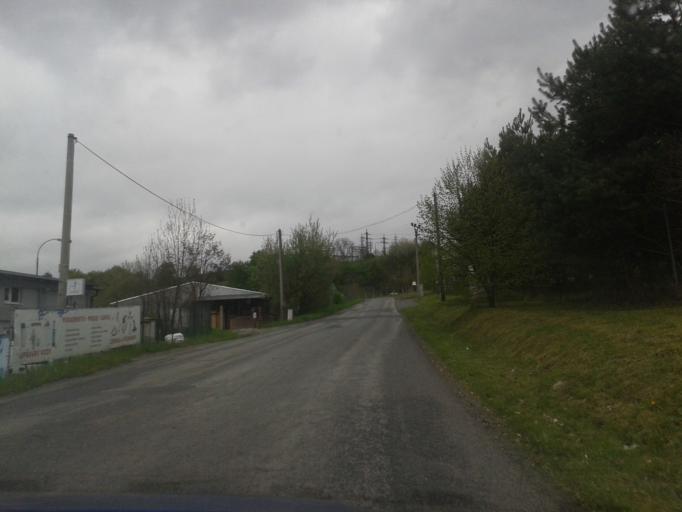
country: CZ
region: Central Bohemia
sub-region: Okres Beroun
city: Beroun
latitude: 49.9556
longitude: 14.0775
